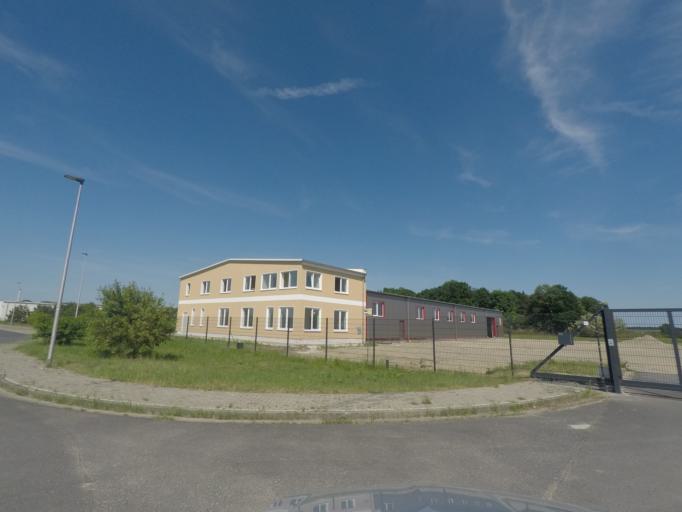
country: DE
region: Brandenburg
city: Eberswalde
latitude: 52.8534
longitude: 13.7883
